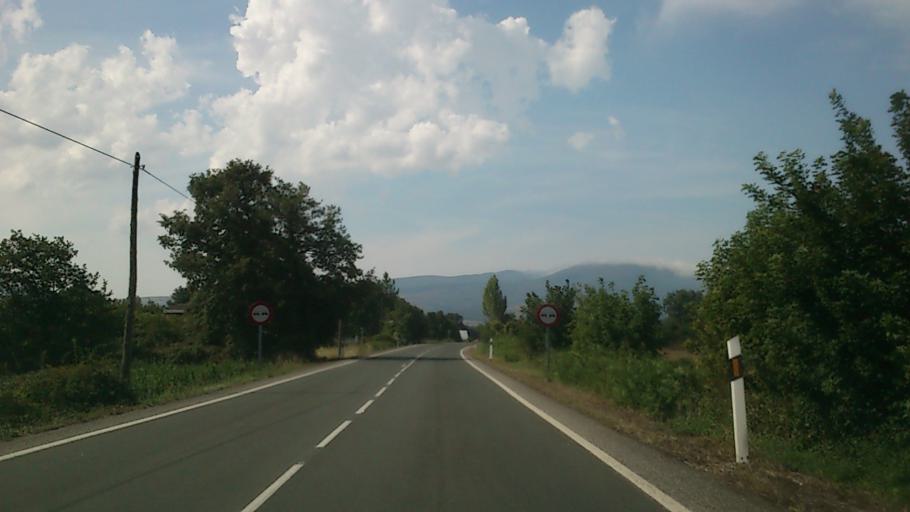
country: ES
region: Castille and Leon
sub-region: Provincia de Burgos
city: Espinosa de los Monteros
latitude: 43.0535
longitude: -3.4903
